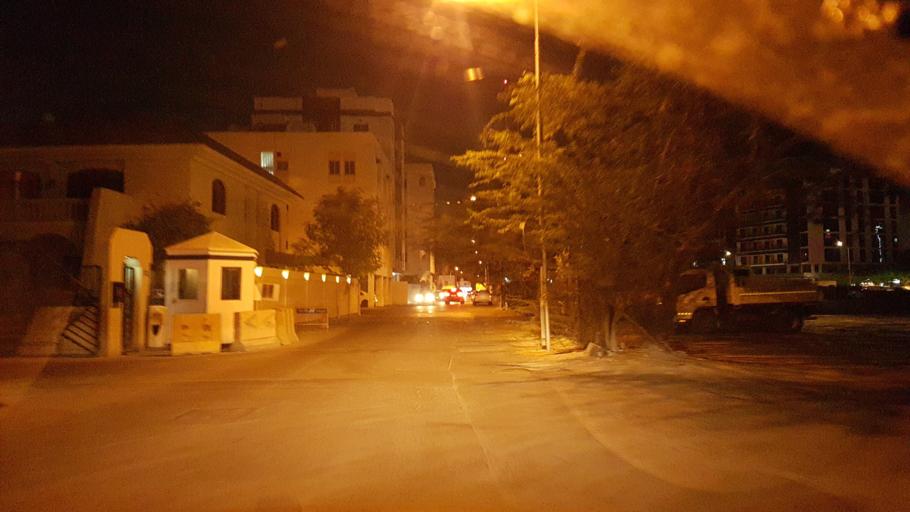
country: BH
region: Manama
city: Manama
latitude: 26.2207
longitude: 50.5868
